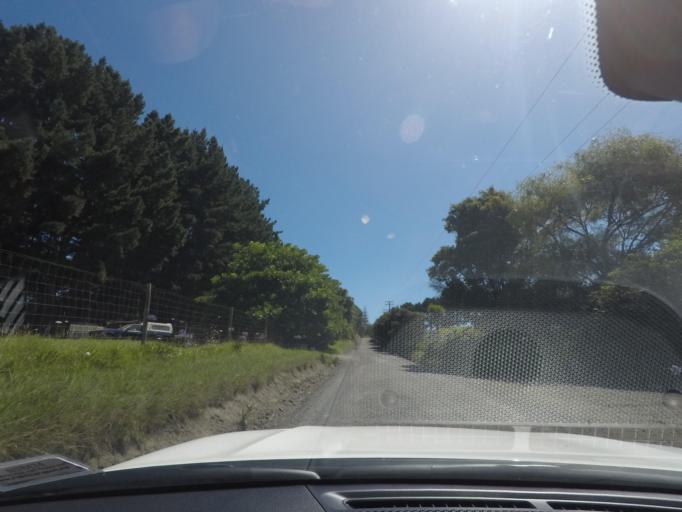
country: NZ
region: Auckland
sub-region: Auckland
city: Parakai
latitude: -36.5803
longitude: 174.3192
